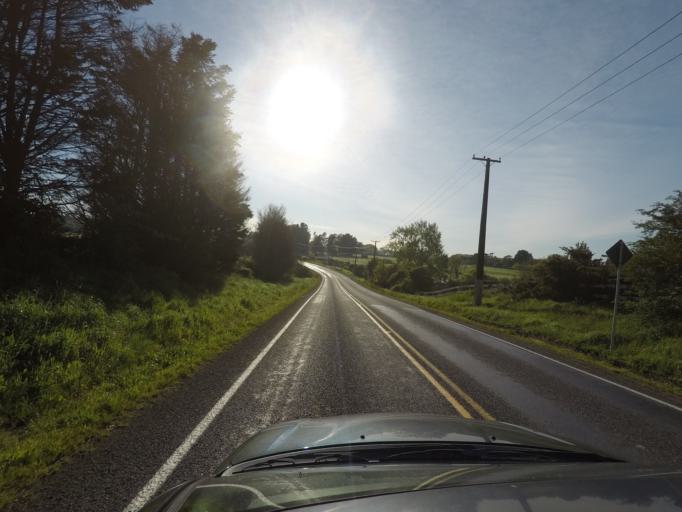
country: NZ
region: Auckland
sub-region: Auckland
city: Takanini
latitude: -37.0181
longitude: 174.9354
